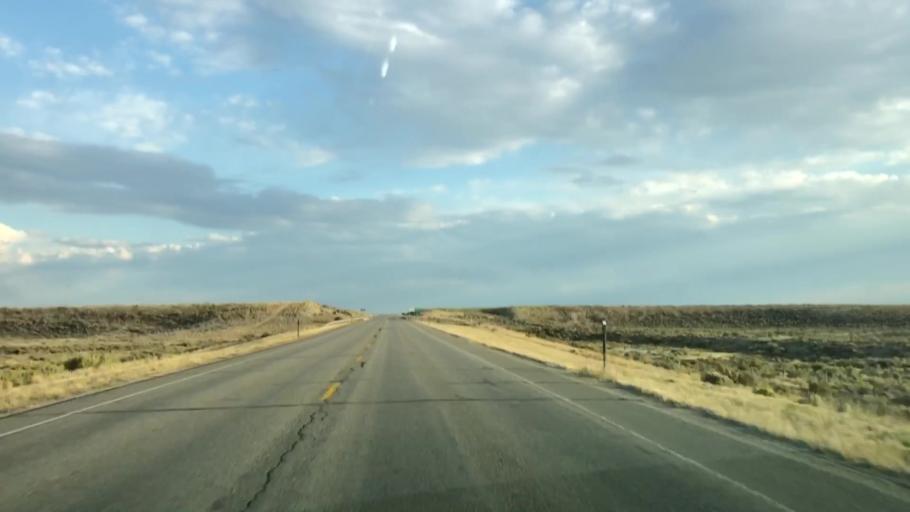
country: US
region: Wyoming
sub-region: Sweetwater County
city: North Rock Springs
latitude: 42.1016
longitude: -109.4464
